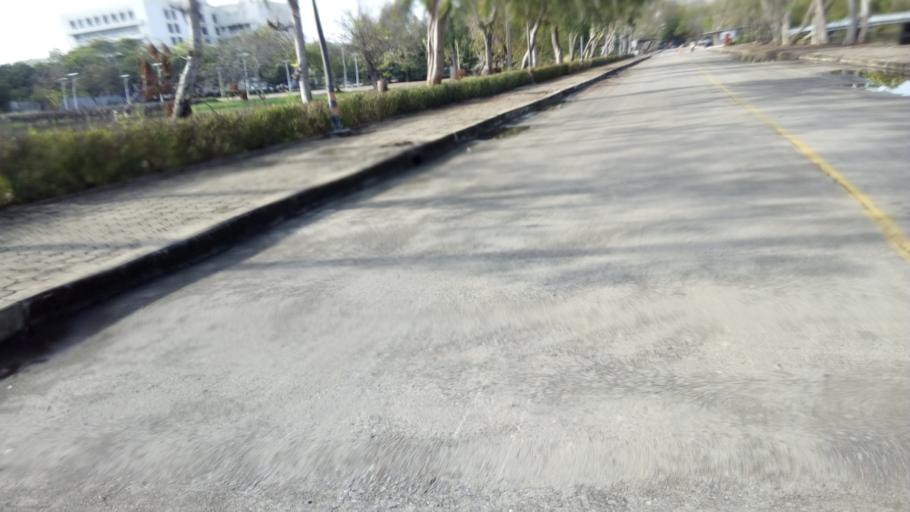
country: TH
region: Nakhon Nayok
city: Ongkharak
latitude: 14.1048
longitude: 100.9872
